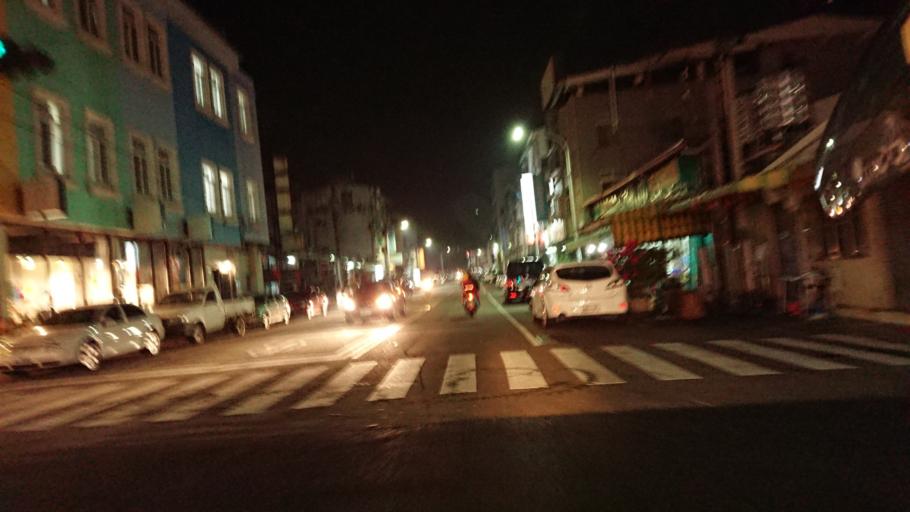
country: TW
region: Taiwan
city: Fengyuan
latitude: 24.2476
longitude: 120.7268
